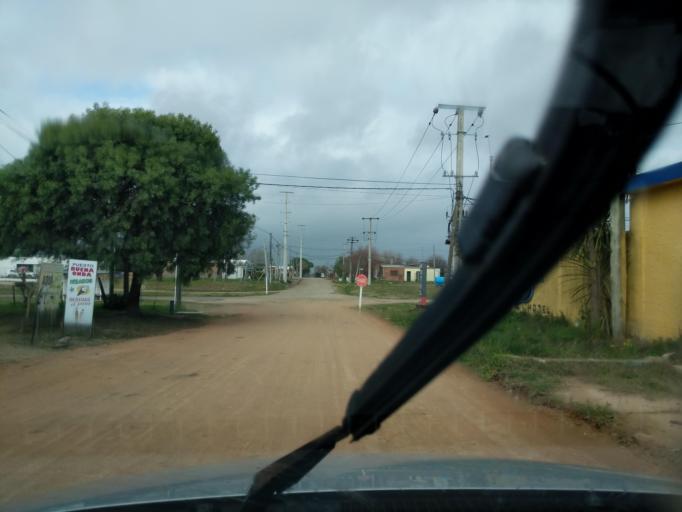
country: UY
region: Florida
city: Florida
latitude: -34.0778
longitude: -56.2227
